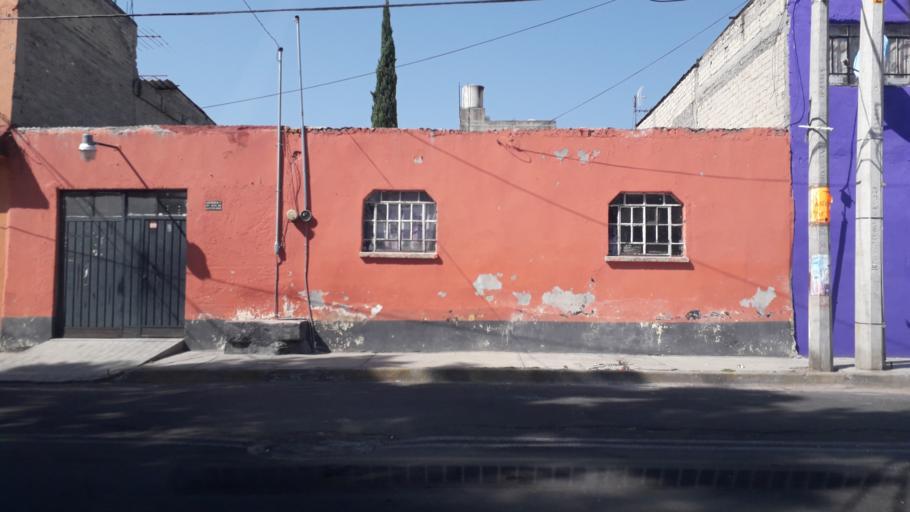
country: MX
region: Mexico City
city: Gustavo A. Madero
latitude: 19.5037
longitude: -99.0974
